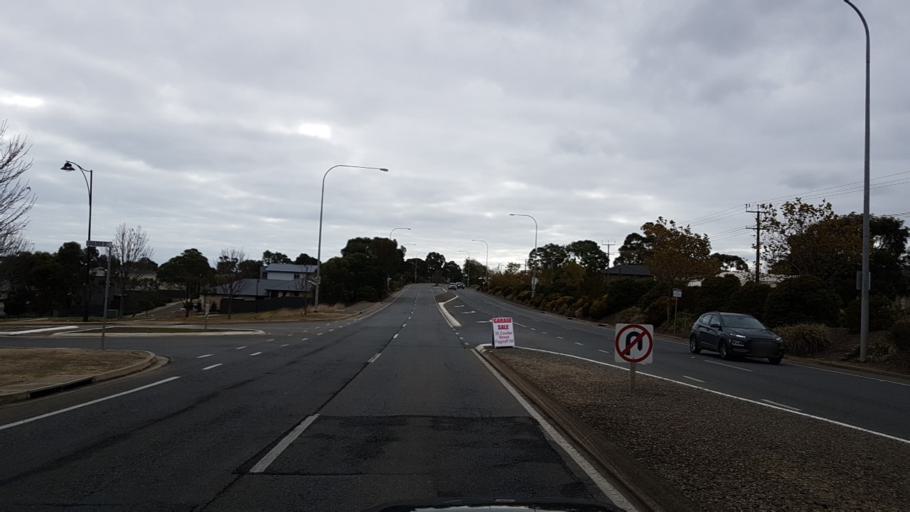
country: AU
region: South Australia
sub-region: Onkaparinga
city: Bedford Park
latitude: -35.0483
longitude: 138.5721
